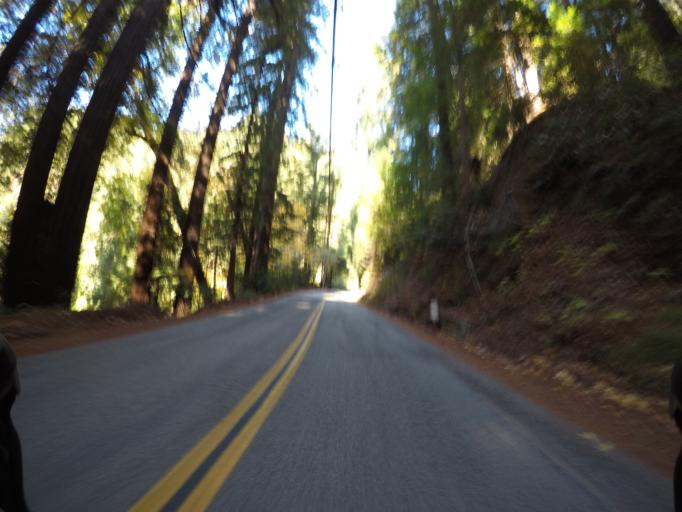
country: US
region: California
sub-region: Santa Cruz County
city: Scotts Valley
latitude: 37.0922
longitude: -122.0049
